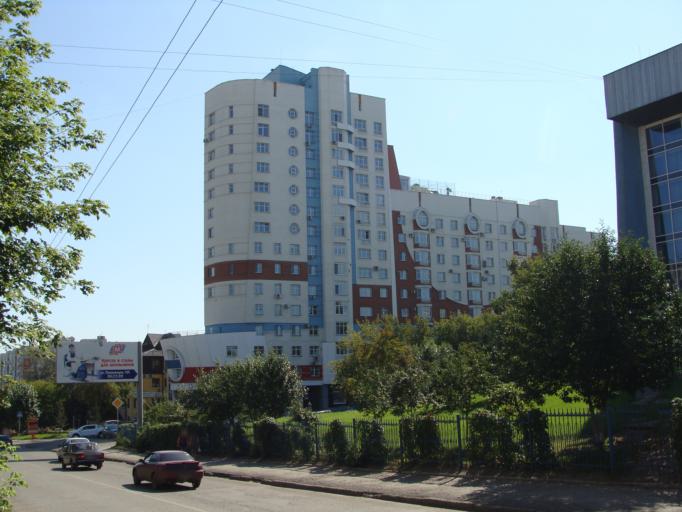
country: RU
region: Altai Krai
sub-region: Gorod Barnaulskiy
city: Barnaul
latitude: 53.3439
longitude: 83.7755
